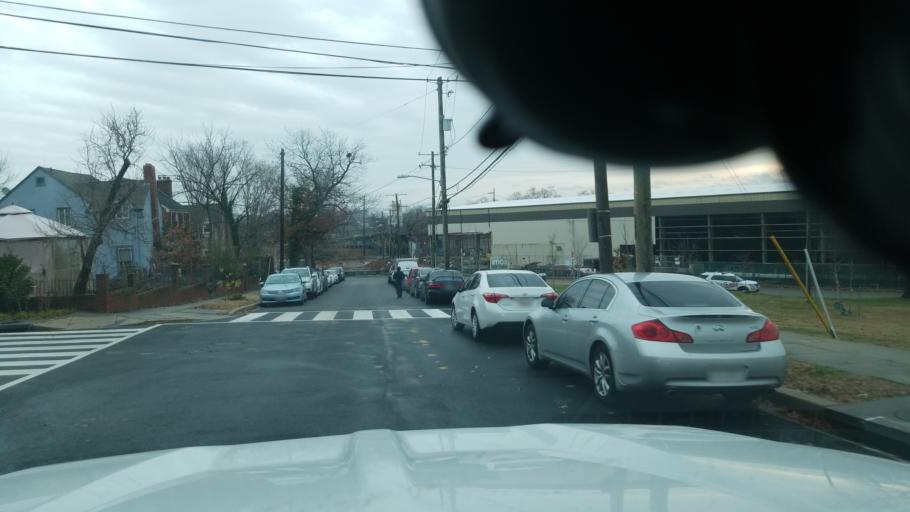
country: US
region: Maryland
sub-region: Prince George's County
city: Mount Rainier
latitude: 38.9213
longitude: -76.9764
